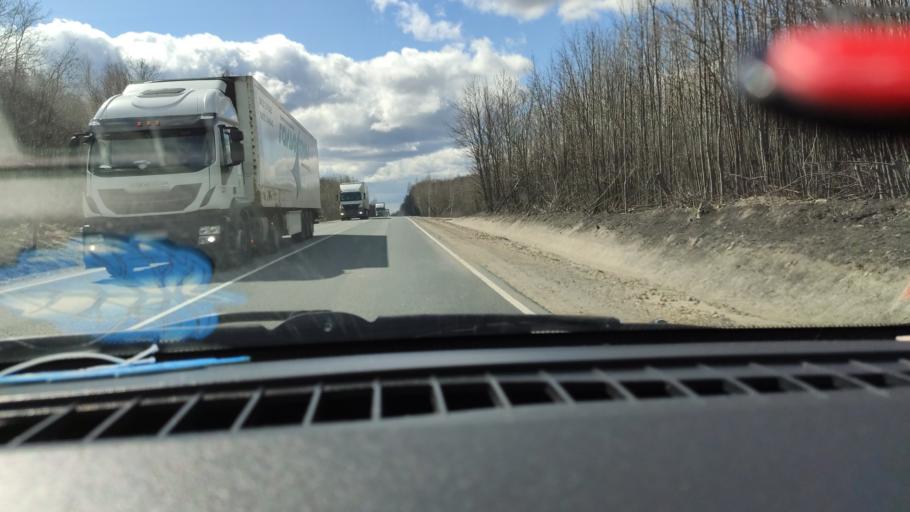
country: RU
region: Saratov
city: Khvalynsk
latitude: 52.4502
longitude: 48.0117
